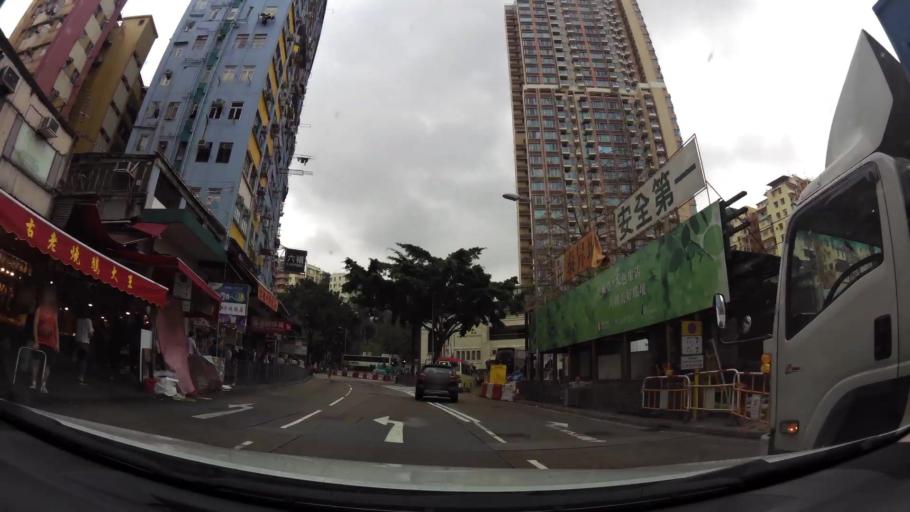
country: HK
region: Kowloon City
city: Kowloon
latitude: 22.3152
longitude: 114.2251
